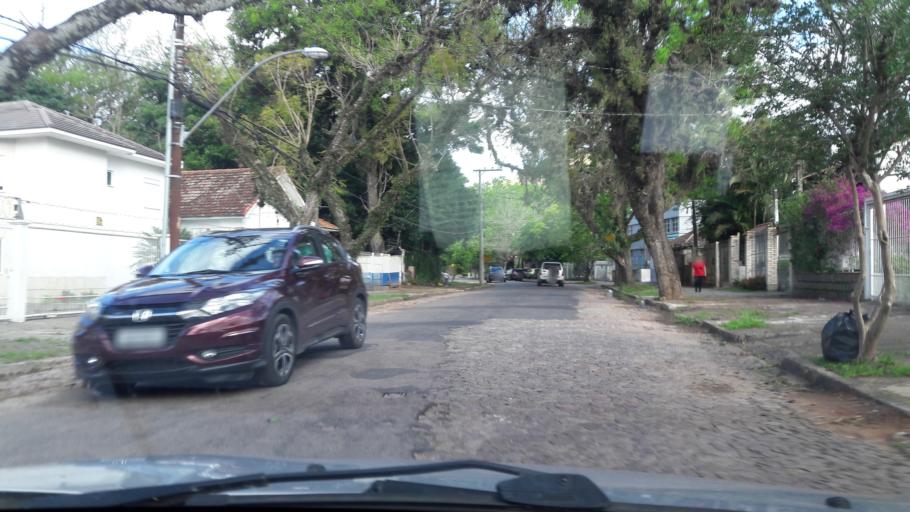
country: BR
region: Rio Grande do Sul
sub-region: Porto Alegre
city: Porto Alegre
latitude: -30.0837
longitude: -51.2069
